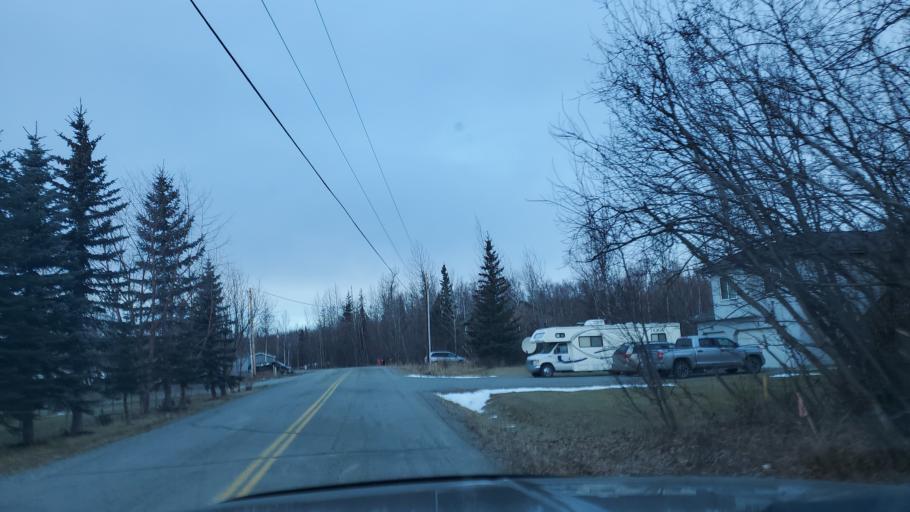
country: US
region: Alaska
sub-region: Matanuska-Susitna Borough
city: Lakes
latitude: 61.5727
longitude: -149.3362
